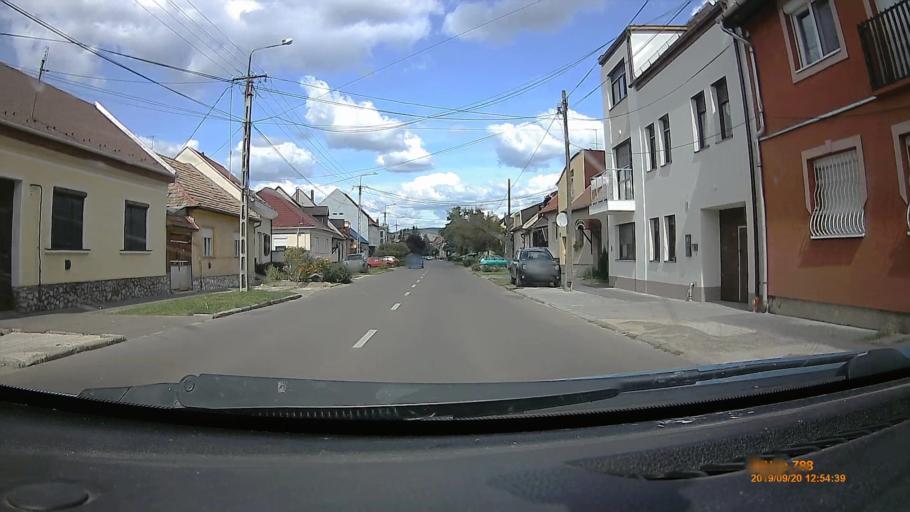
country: HU
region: Heves
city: Eger
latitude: 47.9120
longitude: 20.3766
